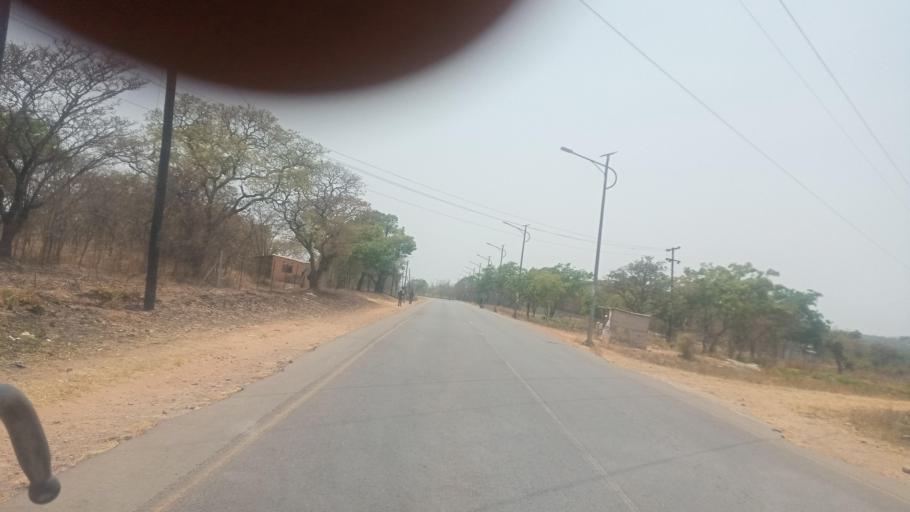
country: ZM
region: Lusaka
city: Lusaka
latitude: -15.4679
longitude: 28.4294
